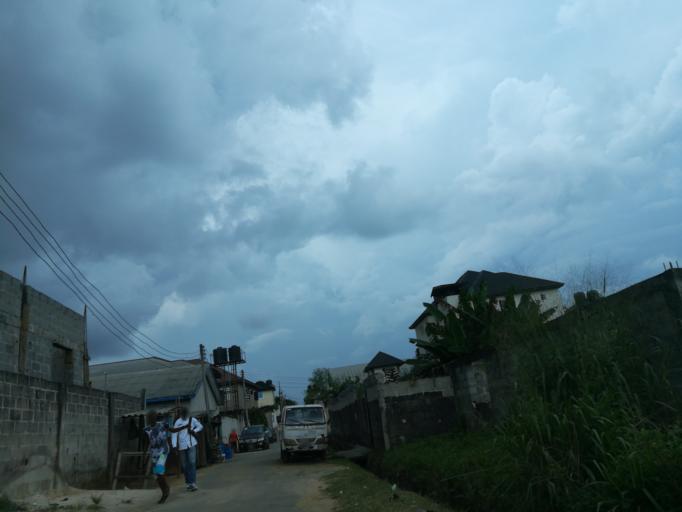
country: NG
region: Rivers
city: Port Harcourt
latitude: 4.8190
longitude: 7.0694
